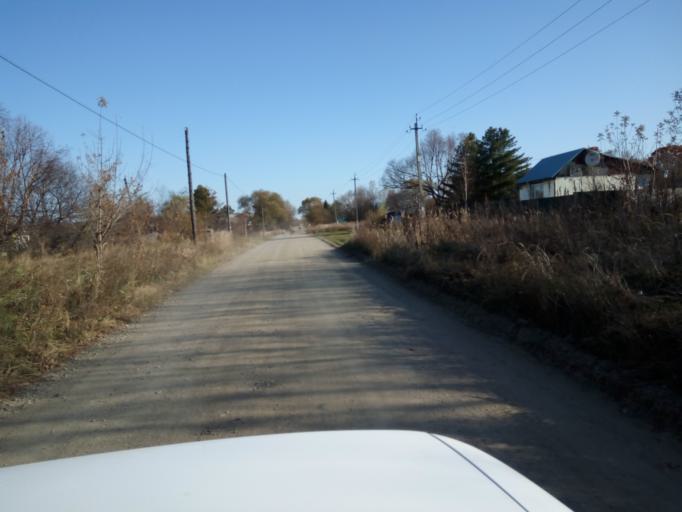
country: RU
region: Primorskiy
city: Lazo
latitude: 45.8704
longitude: 133.6505
